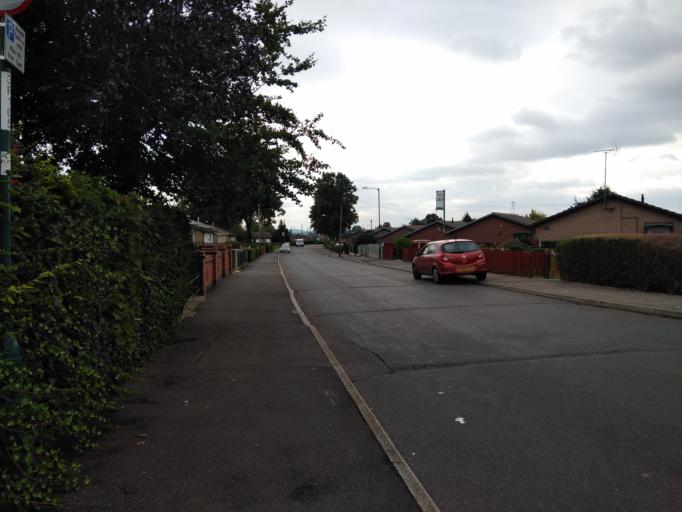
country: GB
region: England
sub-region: Nottingham
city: Nottingham
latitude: 52.9658
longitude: -1.2063
